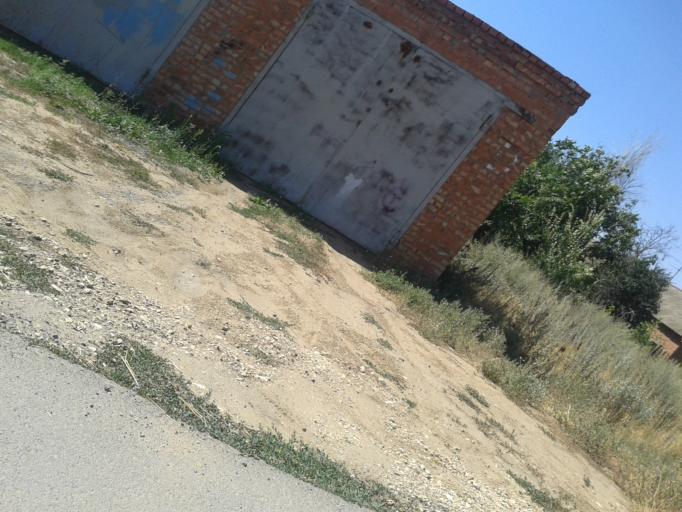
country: RU
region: Volgograd
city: Volgograd
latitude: 48.6912
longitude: 44.4441
